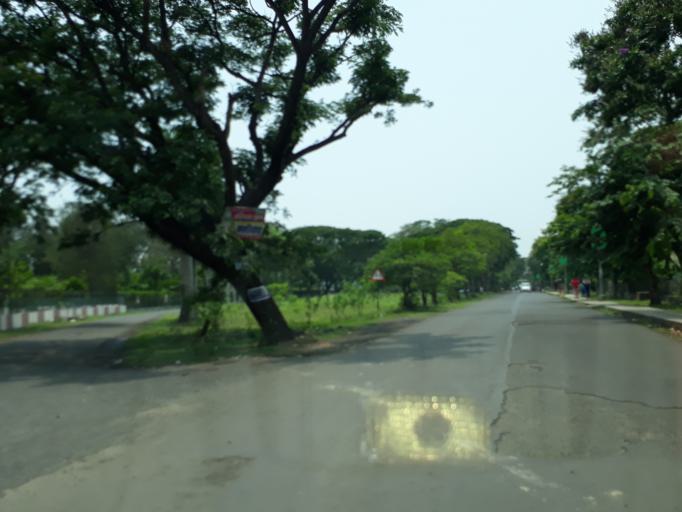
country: IN
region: West Bengal
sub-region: Purba Medinipur
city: Haldia
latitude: 22.0277
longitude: 88.0632
